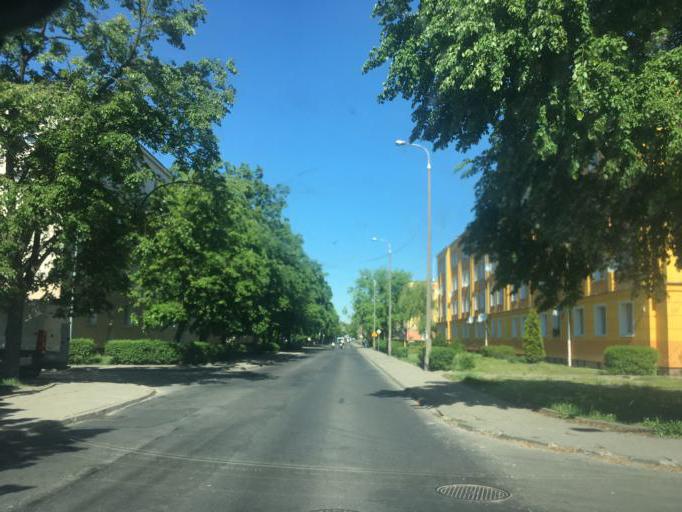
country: PL
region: Kujawsko-Pomorskie
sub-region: Bydgoszcz
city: Bydgoszcz
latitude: 53.1401
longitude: 18.0265
